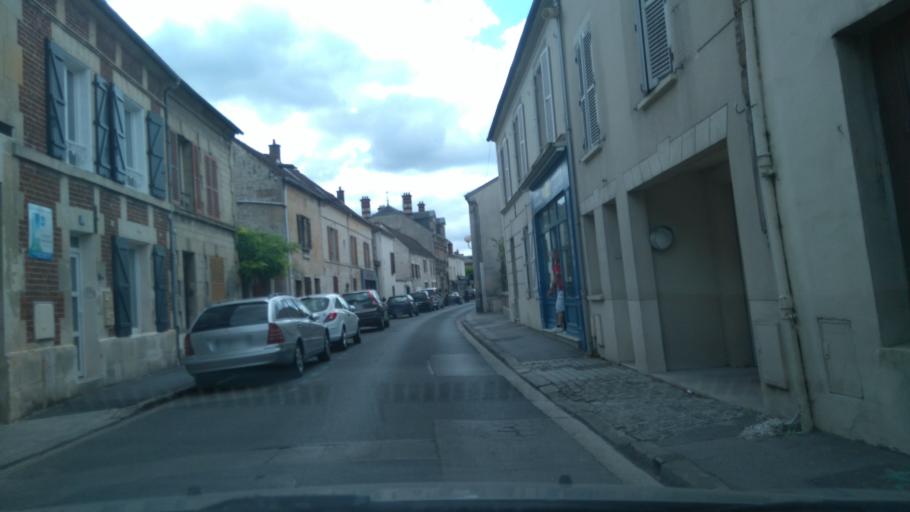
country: FR
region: Picardie
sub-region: Departement de l'Oise
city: Gouvieux
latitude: 49.1860
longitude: 2.4151
